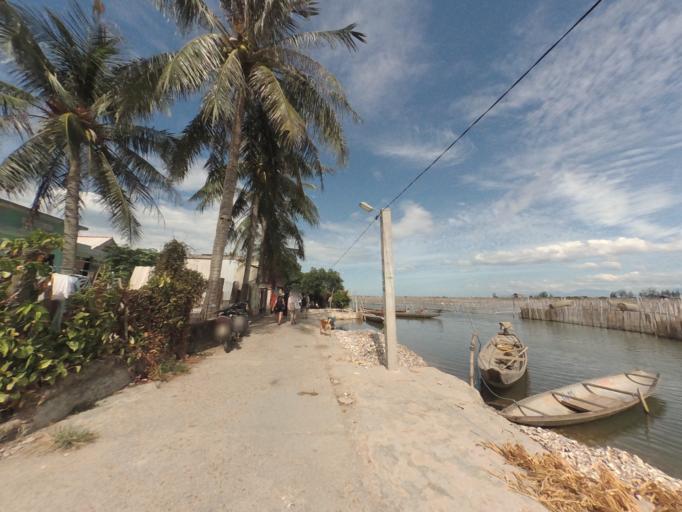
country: VN
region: Thua Thien-Hue
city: Hue
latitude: 16.5375
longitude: 107.6387
